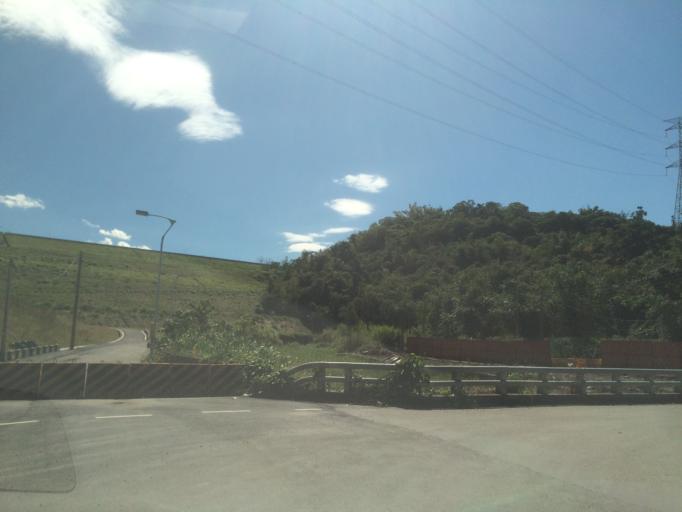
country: TW
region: Taiwan
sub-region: Yunlin
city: Douliu
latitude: 23.6908
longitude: 120.6227
